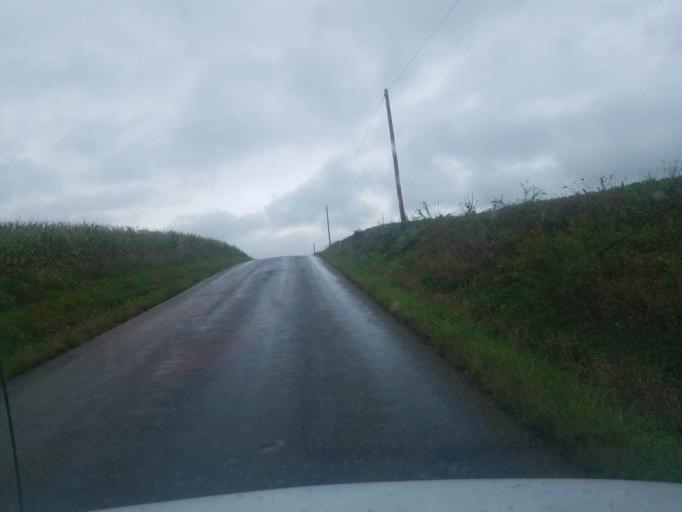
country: US
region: Ohio
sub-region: Wayne County
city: West Salem
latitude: 40.9409
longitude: -82.1188
